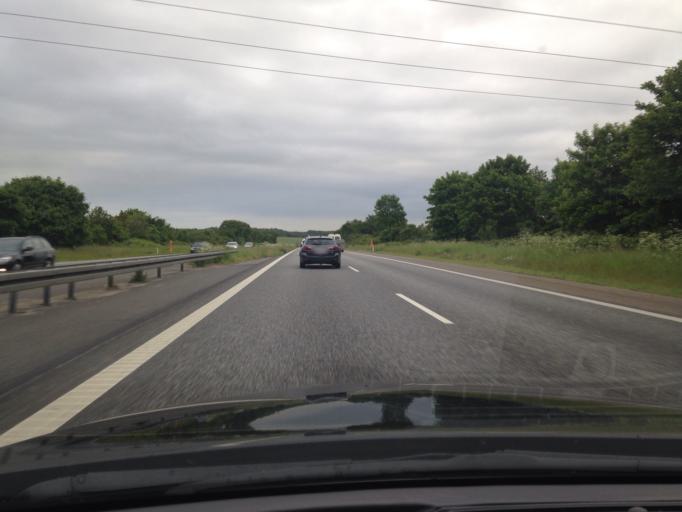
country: DK
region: South Denmark
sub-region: Fredericia Kommune
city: Taulov
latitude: 55.5460
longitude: 9.5596
